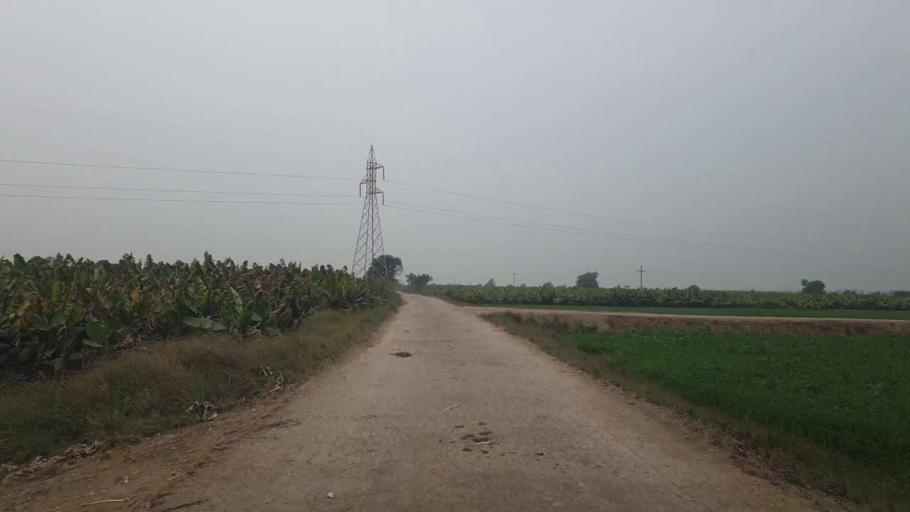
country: PK
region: Sindh
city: Shahdadpur
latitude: 25.8642
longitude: 68.6226
